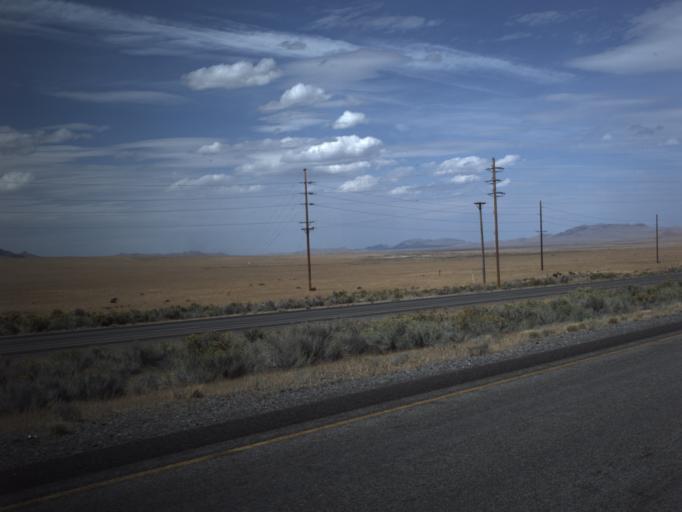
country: US
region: Utah
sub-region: Tooele County
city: Grantsville
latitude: 40.7740
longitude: -112.9761
